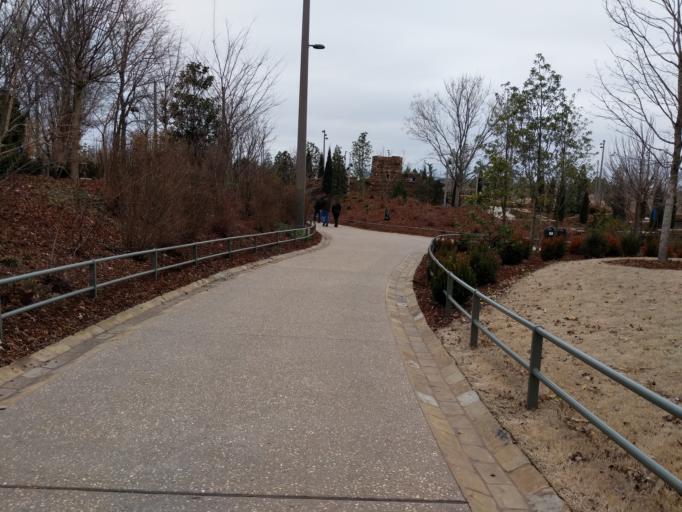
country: US
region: Oklahoma
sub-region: Tulsa County
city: Tulsa
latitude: 36.1248
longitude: -95.9839
